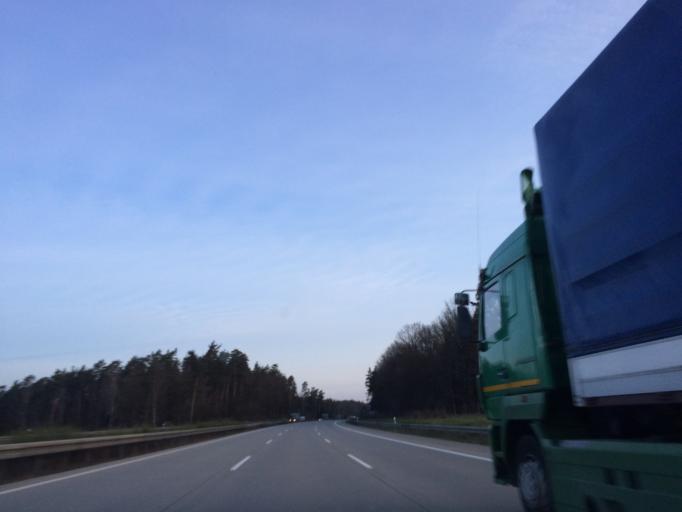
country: DE
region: Thuringia
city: Eineborn
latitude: 50.8411
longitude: 11.8661
